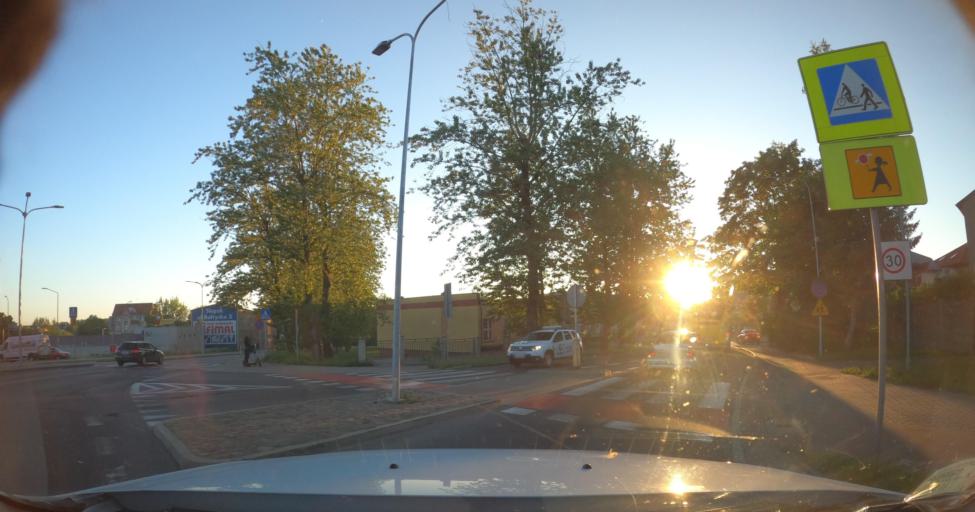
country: PL
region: Pomeranian Voivodeship
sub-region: Slupsk
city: Slupsk
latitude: 54.4656
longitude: 17.0473
